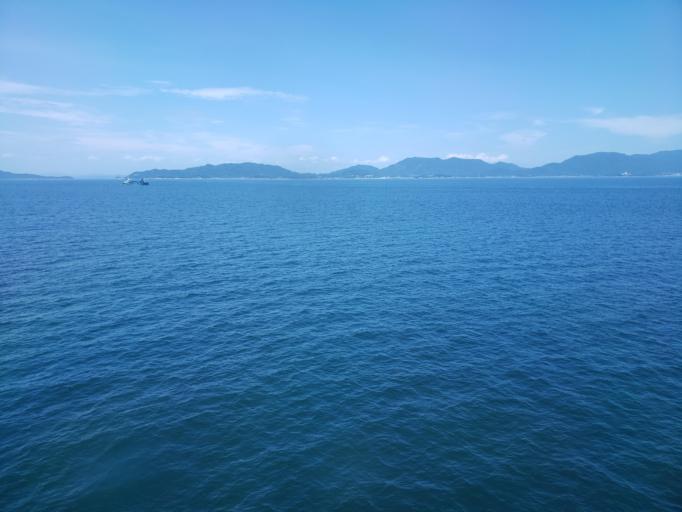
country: JP
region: Kagawa
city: Tonosho
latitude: 34.4065
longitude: 134.1769
